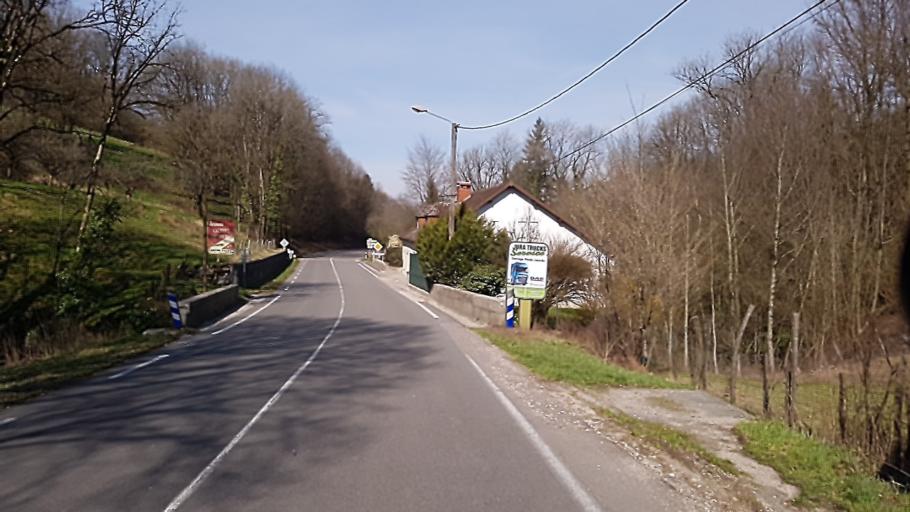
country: FR
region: Franche-Comte
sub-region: Departement du Jura
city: Poligny
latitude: 46.8276
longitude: 5.7209
